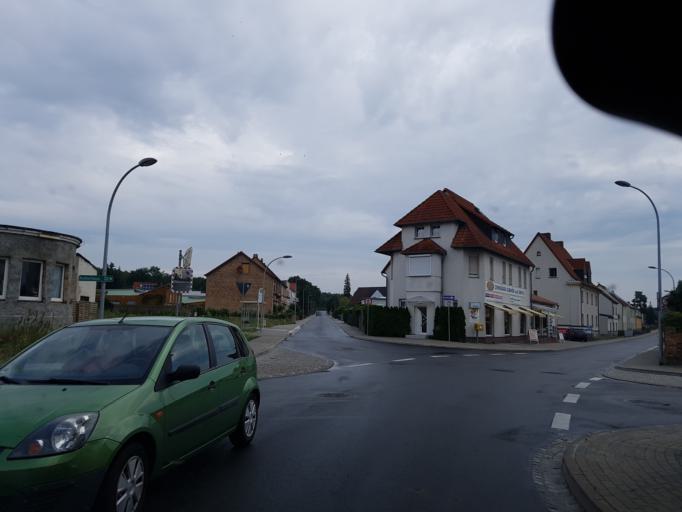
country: DE
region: Brandenburg
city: Senftenberg
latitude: 51.5254
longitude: 13.9451
